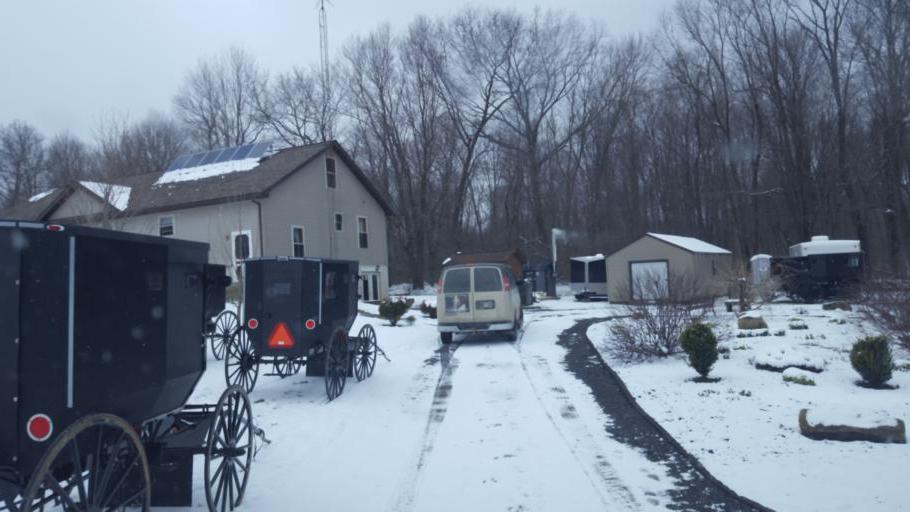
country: US
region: Pennsylvania
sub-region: Crawford County
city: Cochranton
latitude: 41.4309
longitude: -80.0155
